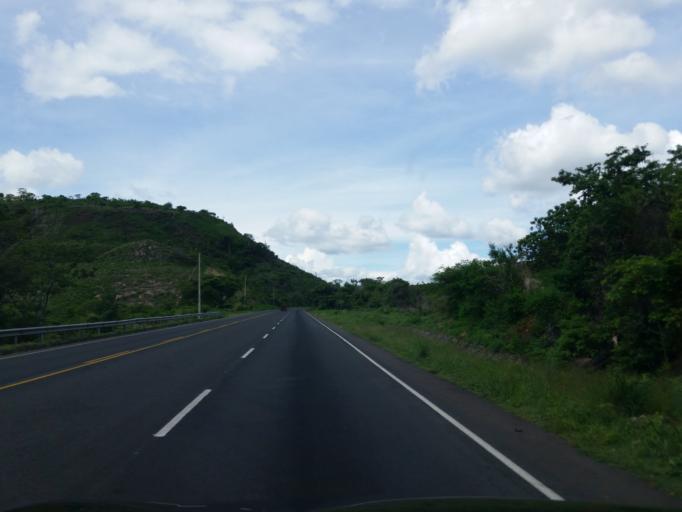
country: NI
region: Managua
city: Valle San Francisco
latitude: 12.4909
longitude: -86.0652
